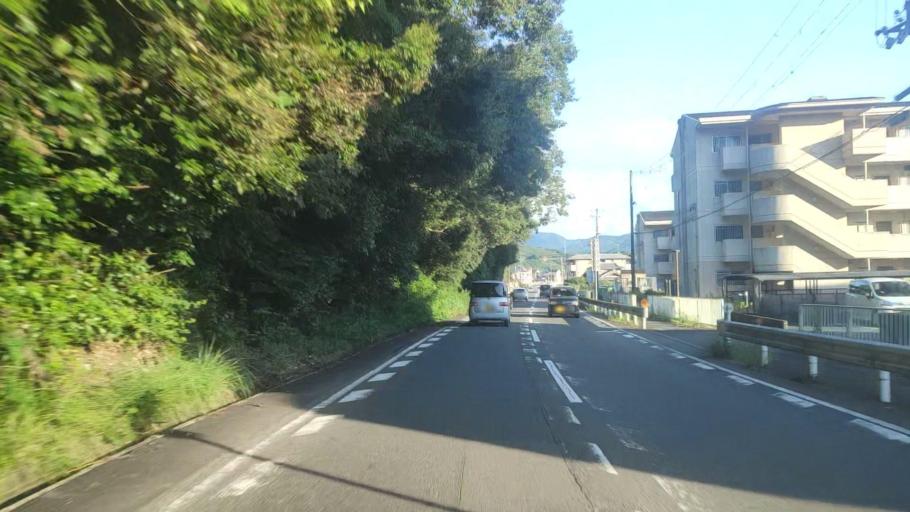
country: JP
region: Wakayama
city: Tanabe
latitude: 33.7244
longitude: 135.4447
